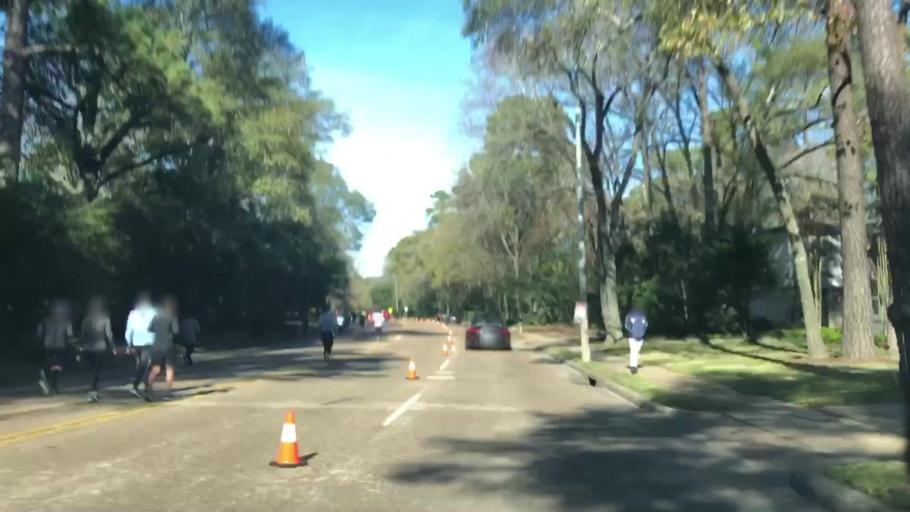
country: US
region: Texas
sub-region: Harris County
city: Hunters Creek Village
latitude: 29.7741
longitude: -95.4805
